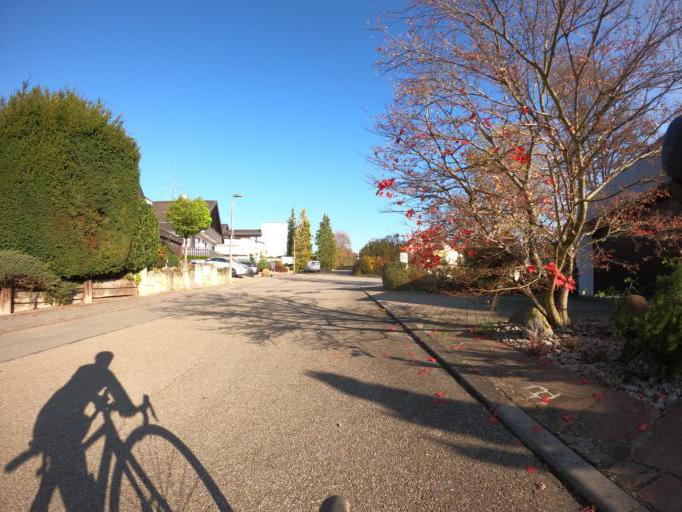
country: DE
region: Baden-Wuerttemberg
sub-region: Regierungsbezirk Stuttgart
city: Aidlingen
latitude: 48.7193
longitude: 8.9097
